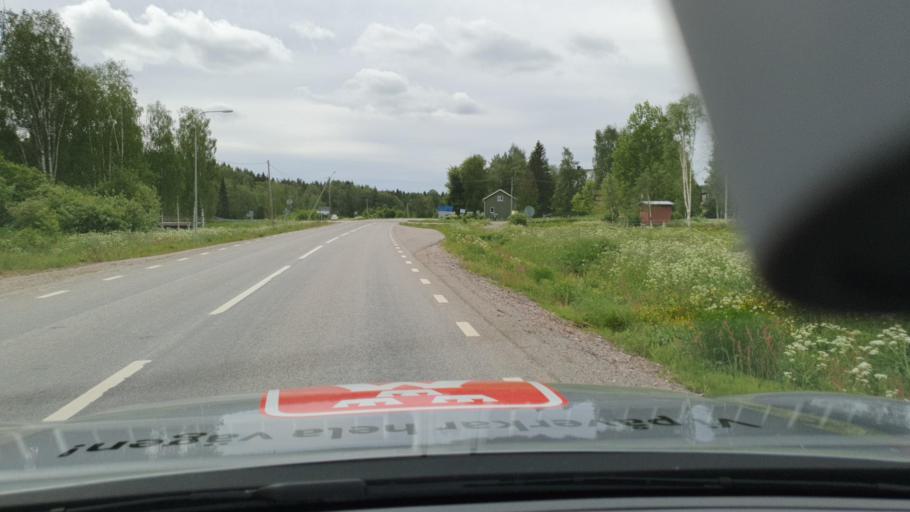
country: SE
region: Norrbotten
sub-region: Kalix Kommun
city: Kalix
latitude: 65.9217
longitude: 23.4601
